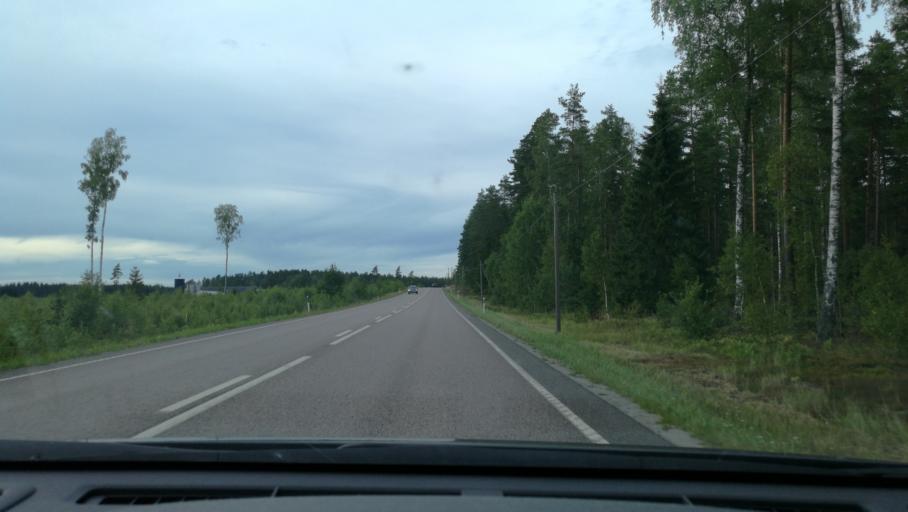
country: SE
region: Soedermanland
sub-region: Katrineholms Kommun
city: Katrineholm
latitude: 59.1959
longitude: 16.1045
